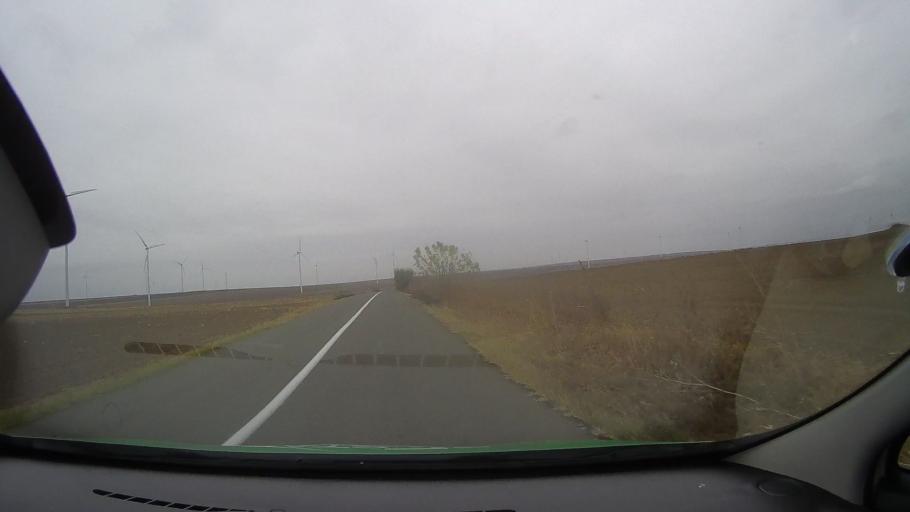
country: RO
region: Constanta
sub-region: Comuna Pantelimon
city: Pantelimon
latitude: 44.5096
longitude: 28.3405
